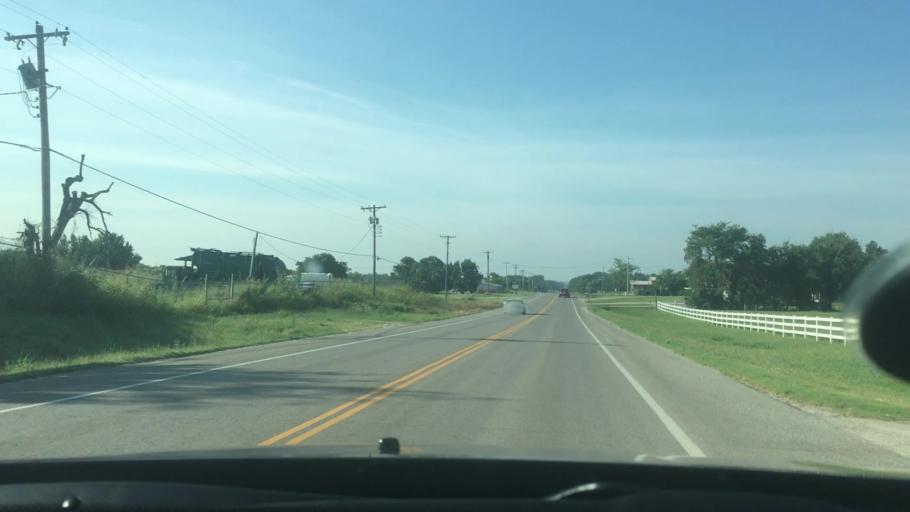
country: US
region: Oklahoma
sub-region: Garvin County
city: Pauls Valley
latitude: 34.7092
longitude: -97.2129
